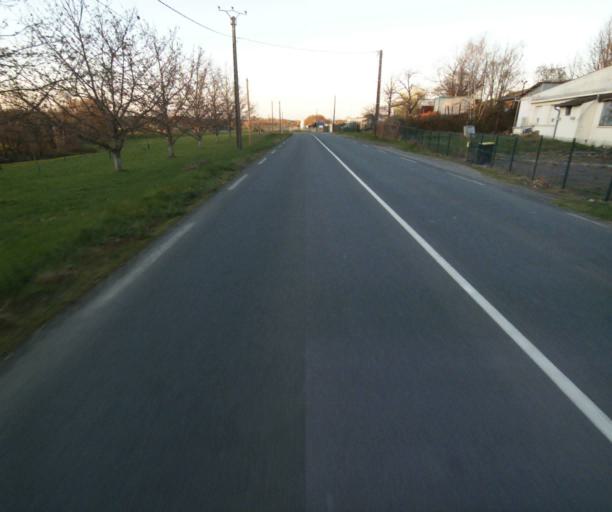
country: FR
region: Limousin
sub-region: Departement de la Correze
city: Sainte-Fereole
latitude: 45.2853
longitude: 1.5678
